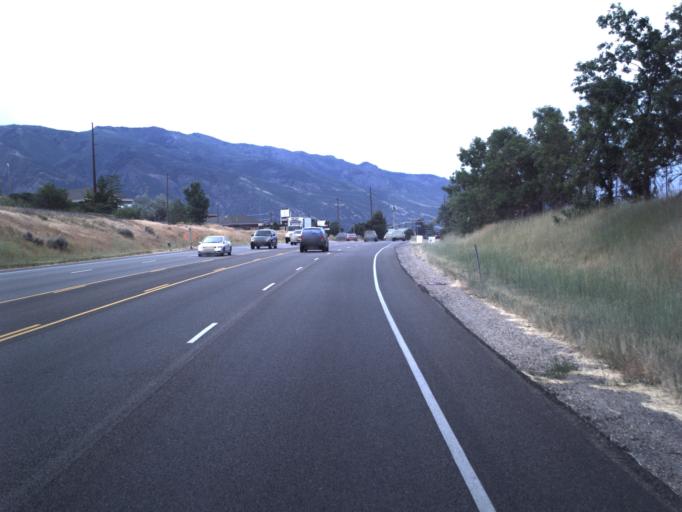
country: US
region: Utah
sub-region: Weber County
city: Uintah
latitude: 41.1641
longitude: -111.9418
